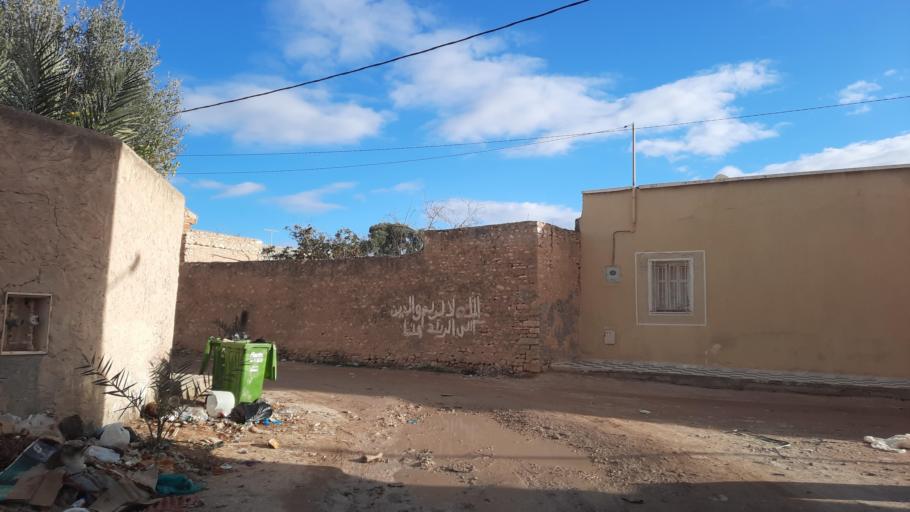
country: TN
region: Al Mahdiyah
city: El Jem
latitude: 35.2915
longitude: 10.7049
